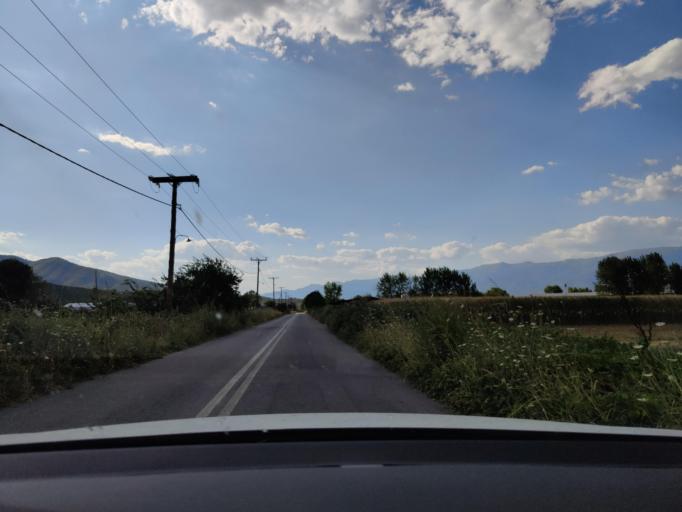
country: GR
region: Central Macedonia
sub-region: Nomos Serron
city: Chrysochorafa
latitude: 41.1796
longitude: 23.1103
